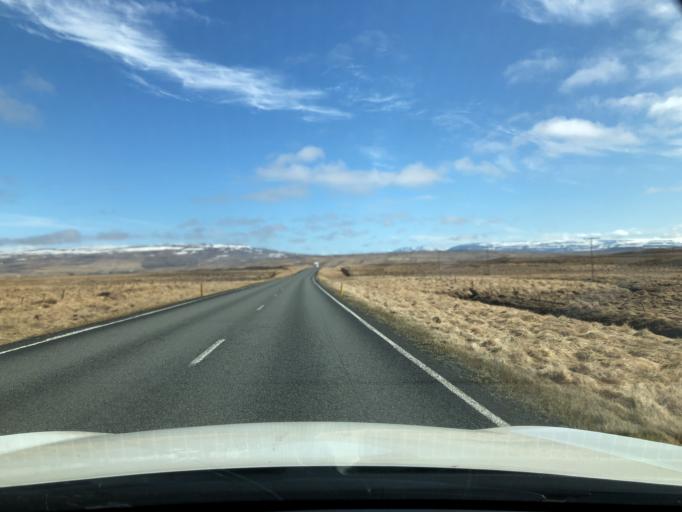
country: IS
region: West
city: Borgarnes
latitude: 65.3084
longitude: -20.9591
